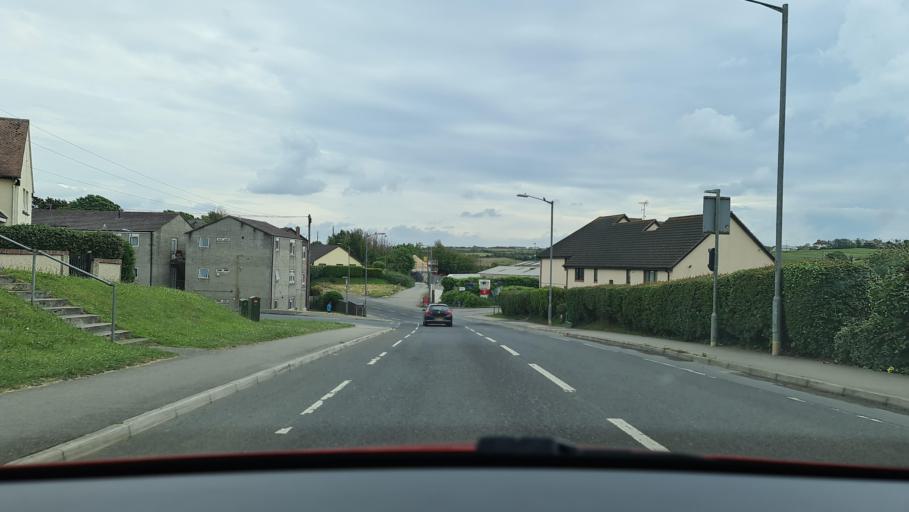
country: GB
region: England
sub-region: Cornwall
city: Bude
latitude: 50.8241
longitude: -4.5412
